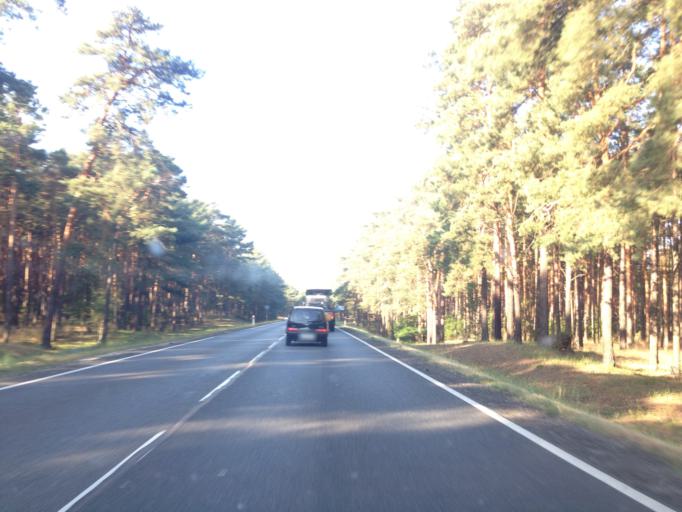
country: PL
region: Kujawsko-Pomorskie
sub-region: Bydgoszcz
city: Bydgoszcz
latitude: 53.0508
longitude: 18.0410
